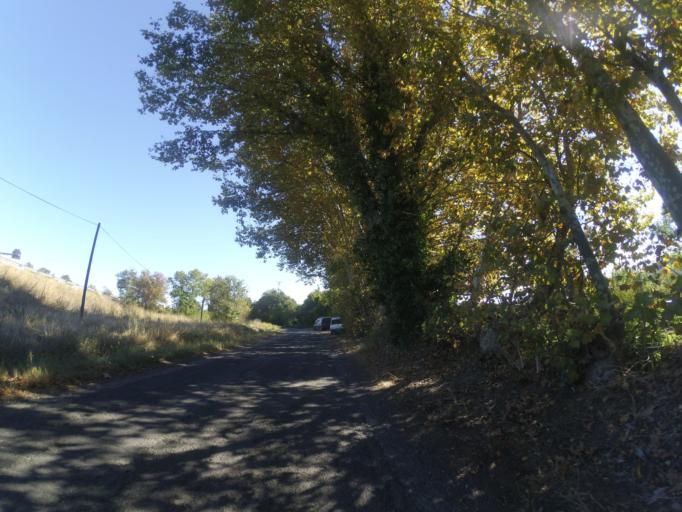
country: FR
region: Languedoc-Roussillon
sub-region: Departement des Pyrenees-Orientales
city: Perpignan
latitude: 42.7084
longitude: 2.8778
